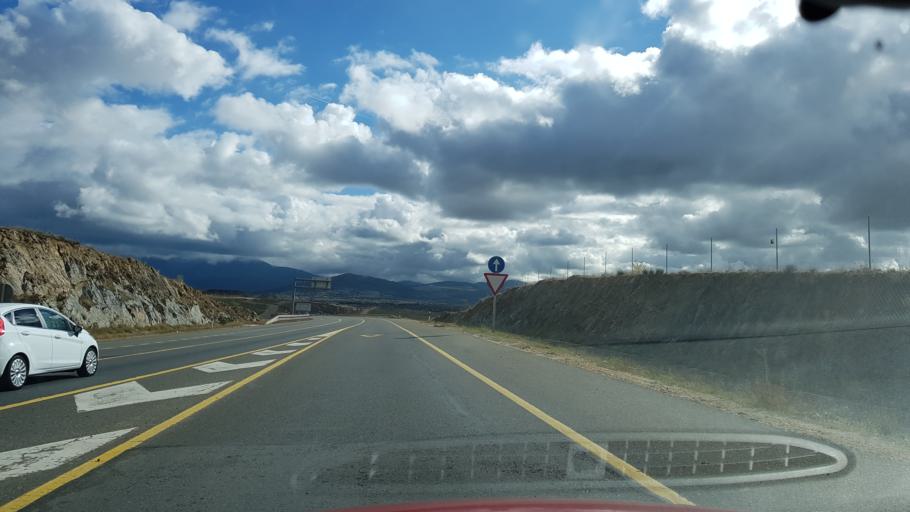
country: ES
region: Castille and Leon
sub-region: Provincia de Segovia
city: San Cristobal de Segovia
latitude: 40.9505
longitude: -4.0905
